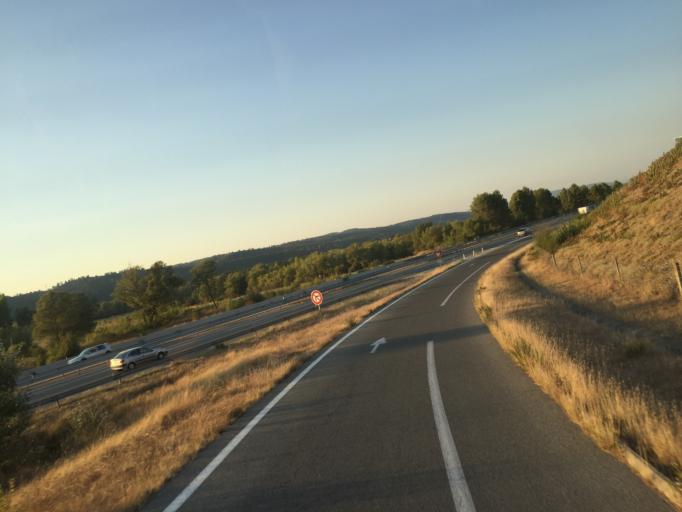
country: FR
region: Provence-Alpes-Cote d'Azur
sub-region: Departement du Vaucluse
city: Beaumont-de-Pertuis
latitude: 43.7050
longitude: 5.7315
